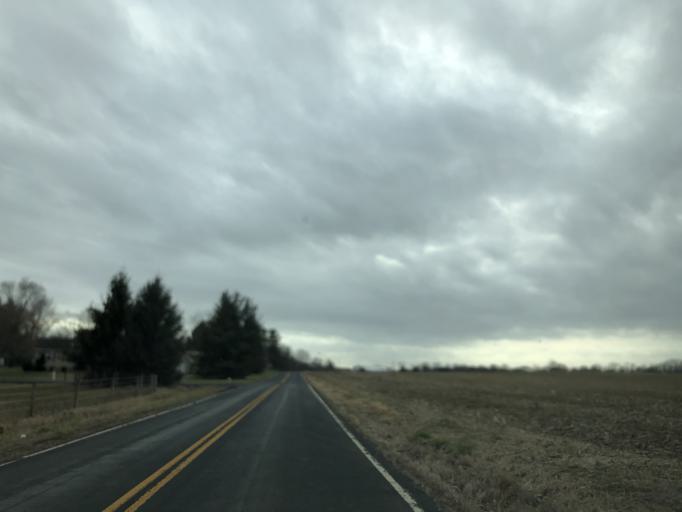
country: US
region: Maryland
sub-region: Cecil County
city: North East
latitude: 39.6744
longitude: -75.9556
